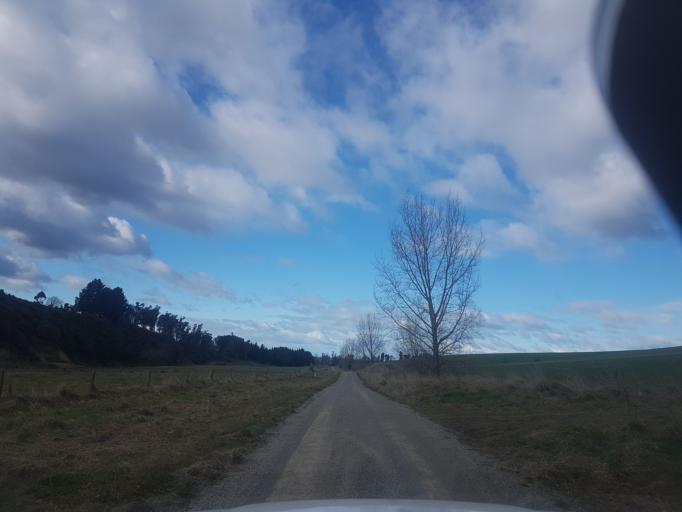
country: NZ
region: Canterbury
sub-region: Timaru District
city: Pleasant Point
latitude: -44.1851
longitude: 171.1456
